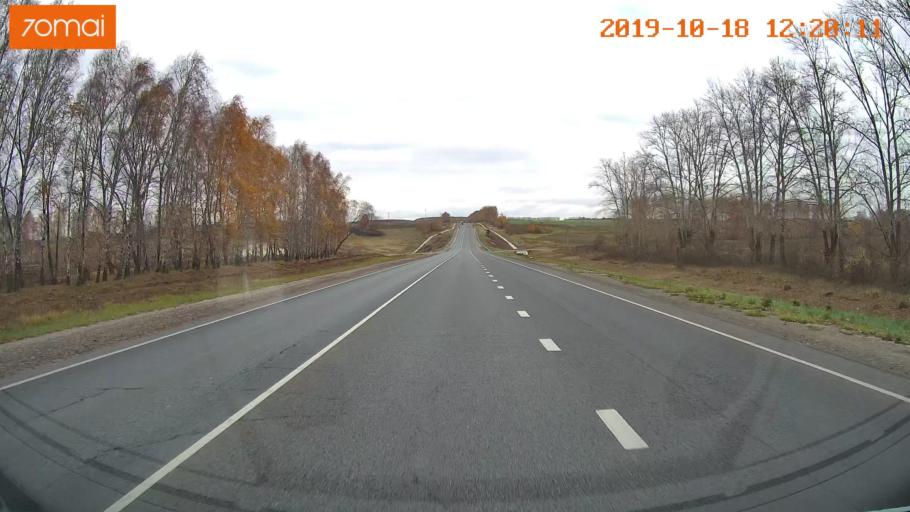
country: RU
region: Rjazan
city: Bagramovo
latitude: 54.4936
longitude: 39.4771
